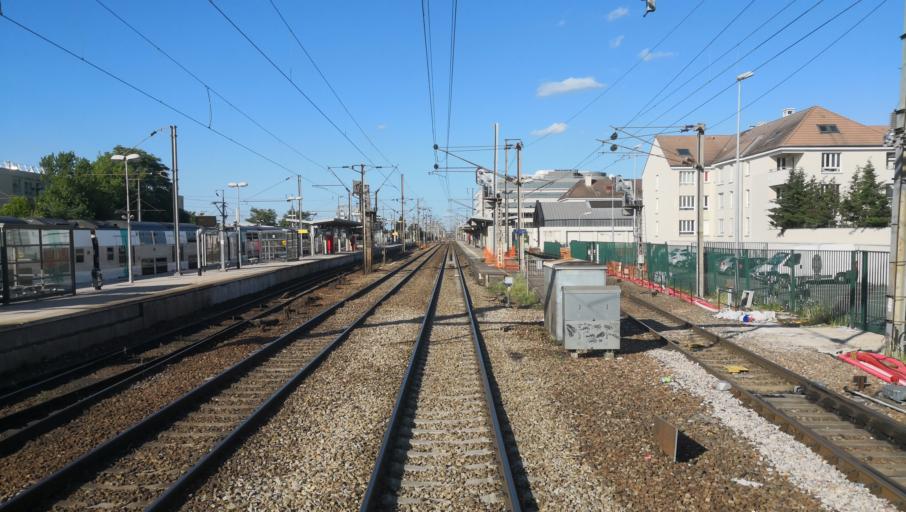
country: FR
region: Ile-de-France
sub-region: Departement des Yvelines
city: Poissy
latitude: 48.9328
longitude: 2.0400
